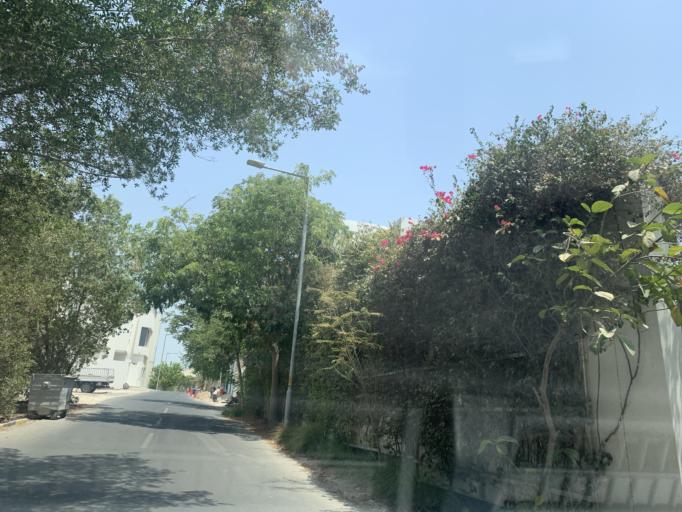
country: BH
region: Manama
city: Jidd Hafs
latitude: 26.2089
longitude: 50.4746
